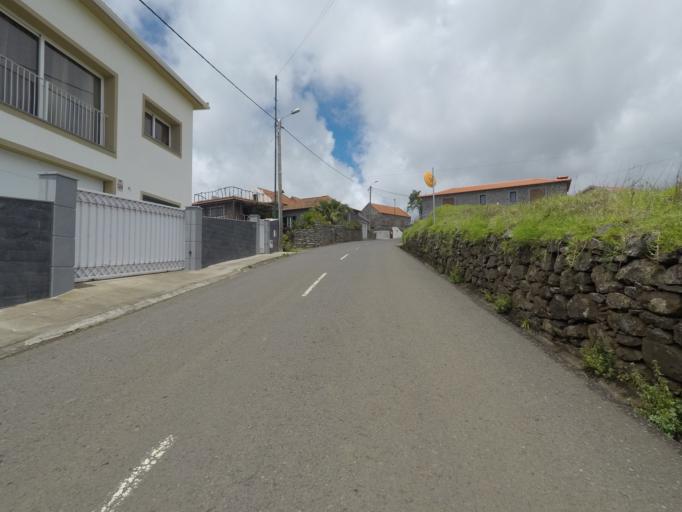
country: PT
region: Madeira
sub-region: Calheta
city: Faja da Ovelha
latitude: 32.7532
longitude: -17.2143
